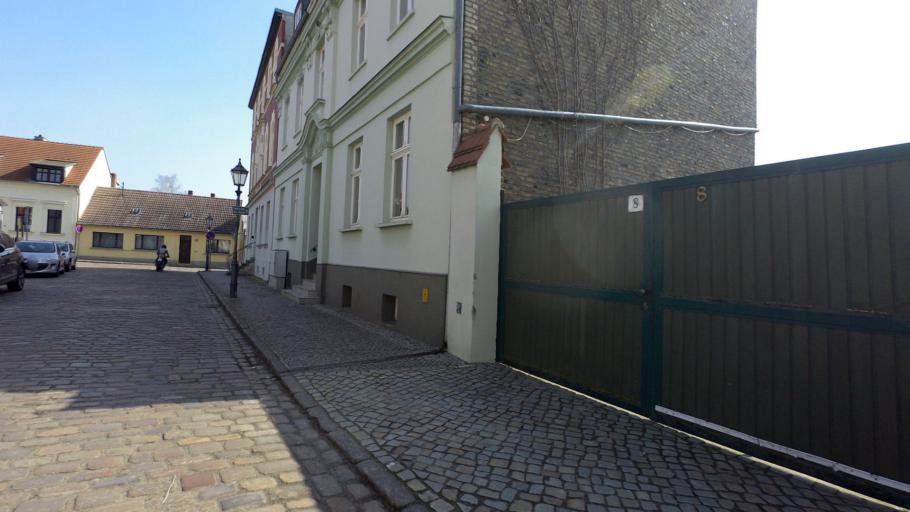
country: DE
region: Brandenburg
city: Werder
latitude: 52.3798
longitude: 12.9436
